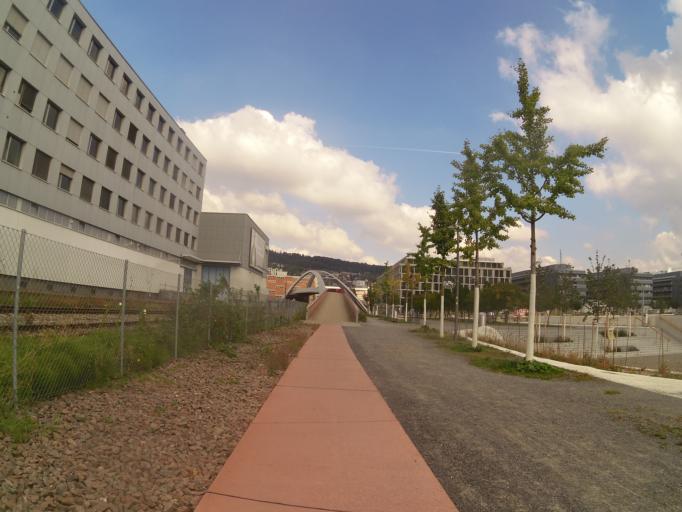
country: CH
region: Zurich
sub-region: Bezirk Zuerich
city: Zuerich (Kreis 5) / Escher-Wyss
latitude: 47.3883
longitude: 8.5123
